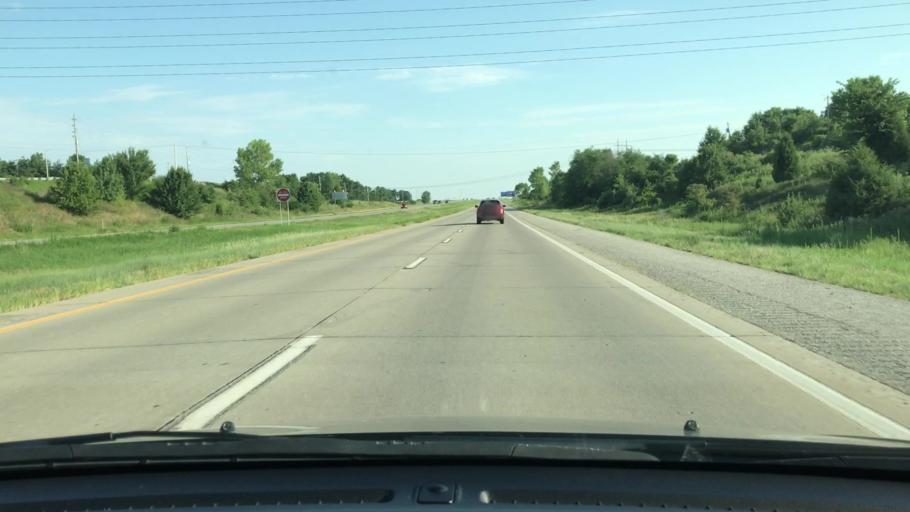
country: US
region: Missouri
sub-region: Jackson County
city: Greenwood
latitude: 38.8666
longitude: -94.3752
